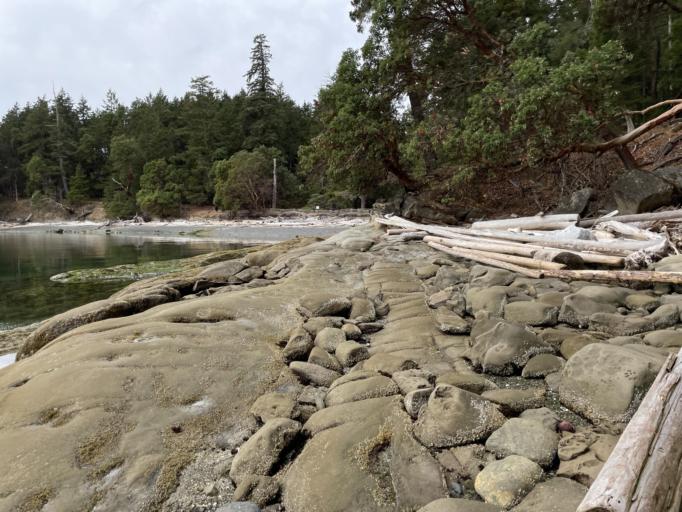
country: CA
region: British Columbia
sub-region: Cowichan Valley Regional District
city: Ladysmith
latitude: 49.0940
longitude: -123.7245
